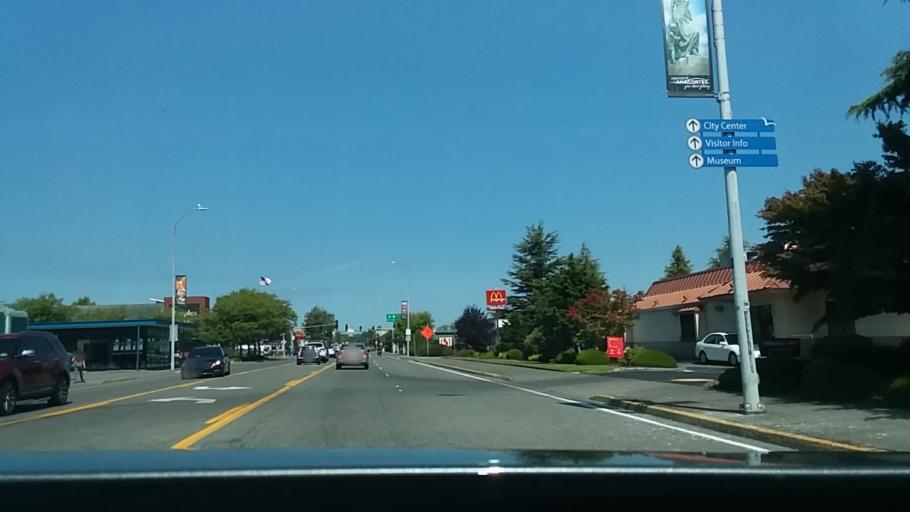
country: US
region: Washington
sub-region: Skagit County
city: Anacortes
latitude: 48.5110
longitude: -122.6125
